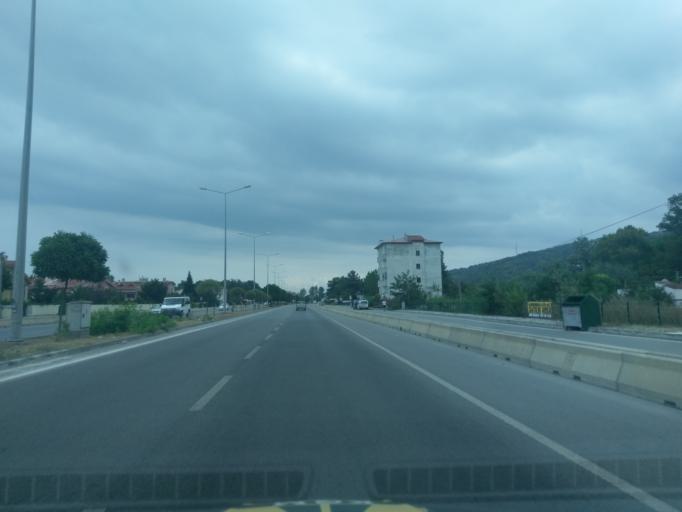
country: TR
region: Samsun
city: Taflan
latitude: 41.3979
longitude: 36.1950
